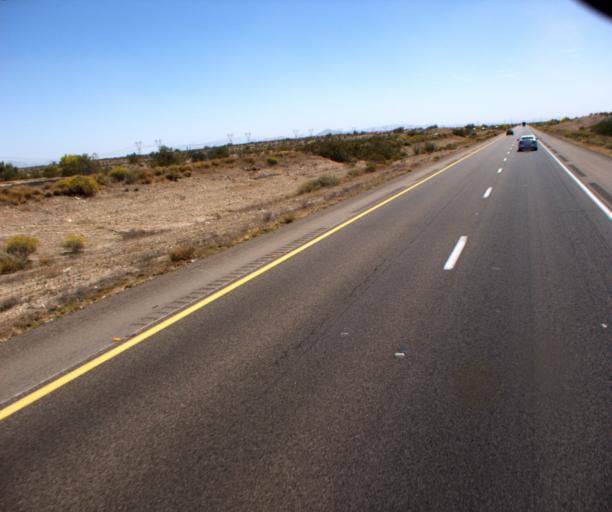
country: US
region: Arizona
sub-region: Maricopa County
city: Gila Bend
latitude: 33.0659
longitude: -112.6456
